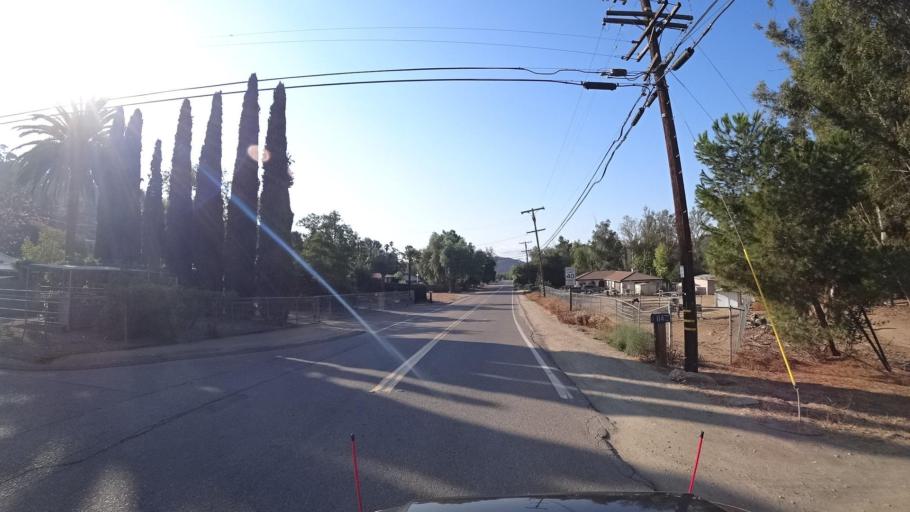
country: US
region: California
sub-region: San Diego County
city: Eucalyptus Hills
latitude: 32.8861
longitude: -116.9549
